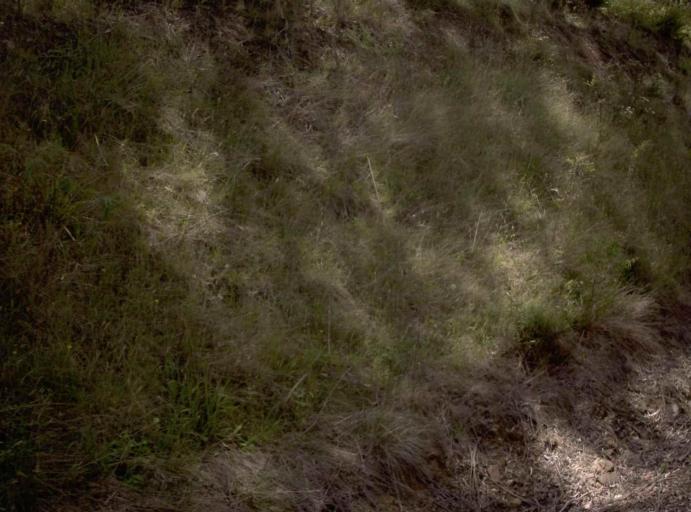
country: AU
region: New South Wales
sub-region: Bombala
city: Bombala
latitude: -37.3692
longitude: 149.0165
